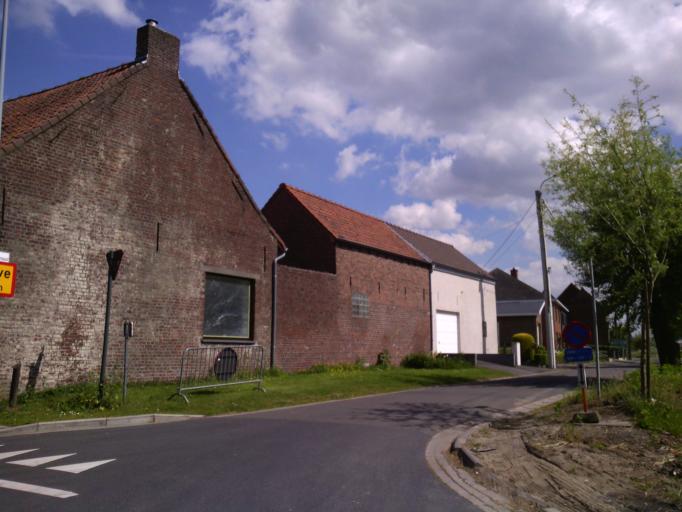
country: BE
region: Flanders
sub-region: Provincie West-Vlaanderen
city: Wevelgem
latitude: 50.7908
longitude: 3.1718
